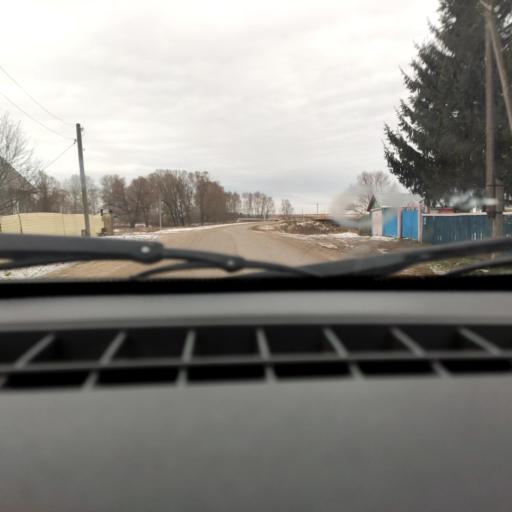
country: RU
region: Bashkortostan
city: Tolbazy
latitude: 54.2531
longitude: 55.9172
